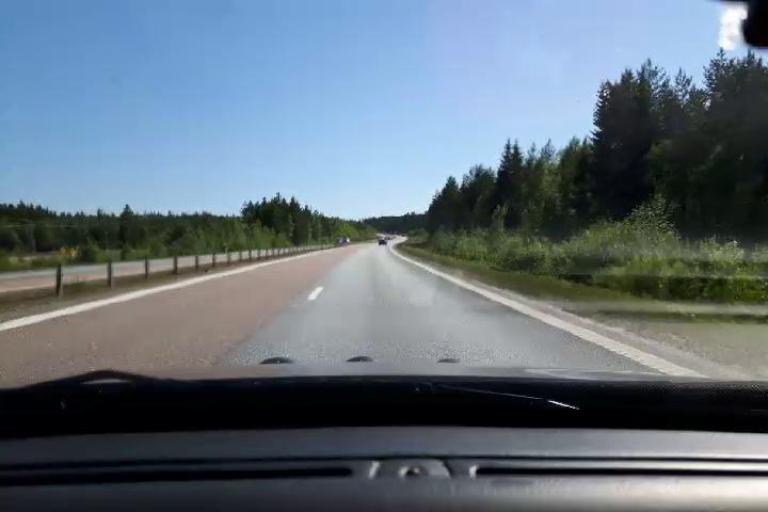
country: SE
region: Gaevleborg
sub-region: Soderhamns Kommun
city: Soderhamn
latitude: 61.4045
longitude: 16.9938
